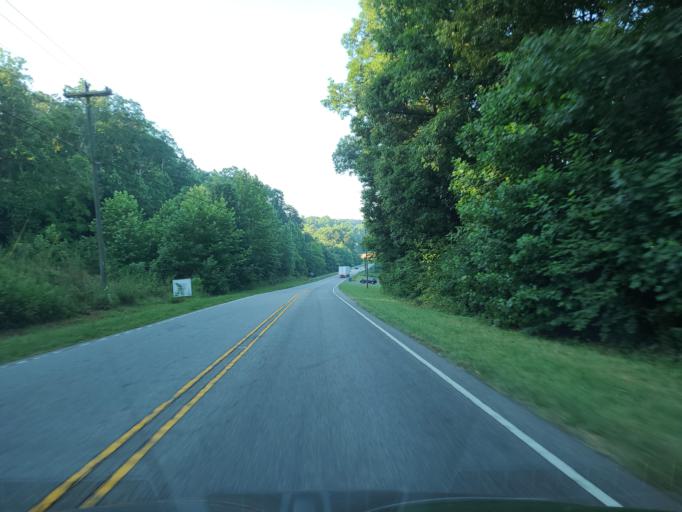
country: US
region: North Carolina
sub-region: Catawba County
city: Mountain View
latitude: 35.6480
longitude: -81.3807
